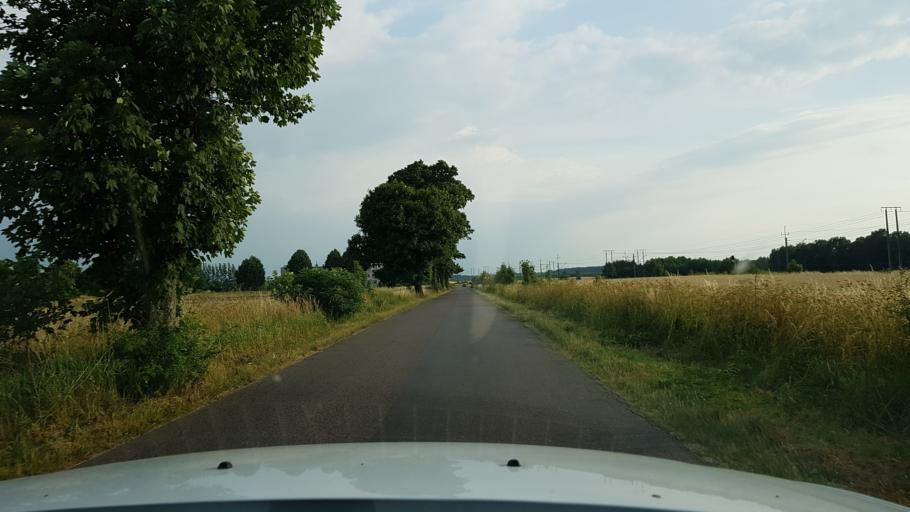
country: PL
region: West Pomeranian Voivodeship
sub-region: Powiat swidwinski
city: Swidwin
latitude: 53.8035
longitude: 15.7893
